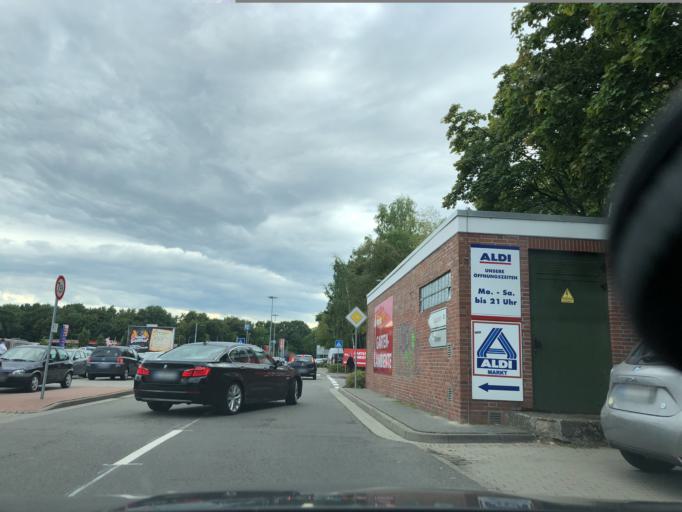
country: DE
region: Lower Saxony
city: Oldenburg
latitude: 53.1604
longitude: 8.1747
